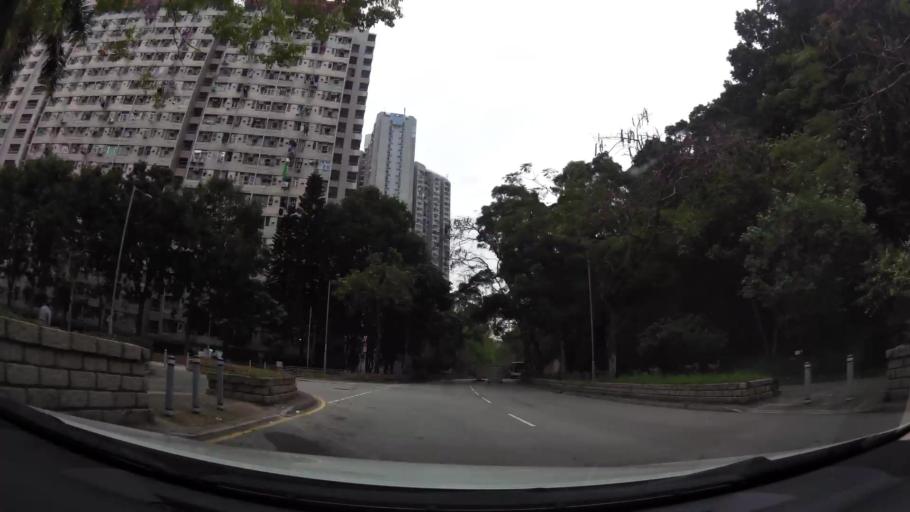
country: HK
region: Tai Po
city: Tai Po
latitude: 22.4586
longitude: 114.1724
